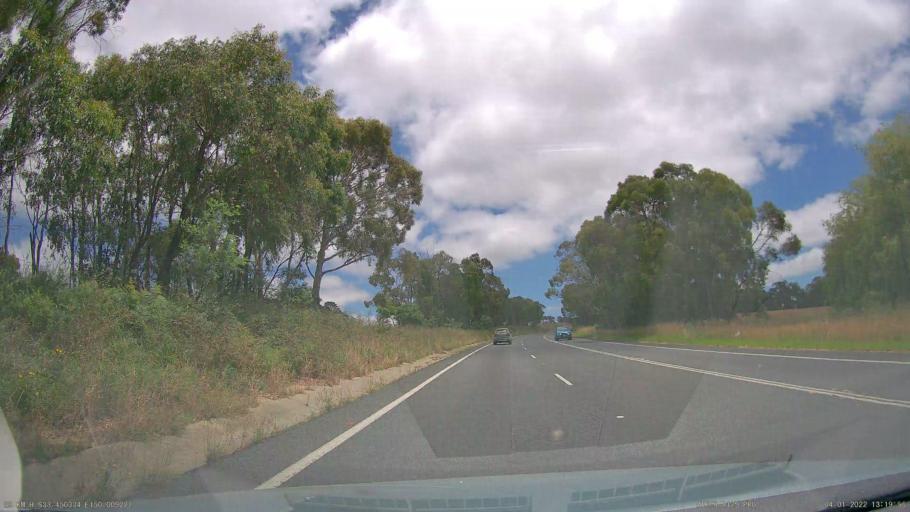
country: AU
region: New South Wales
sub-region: Lithgow
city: Portland
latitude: -33.4503
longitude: 150.0087
